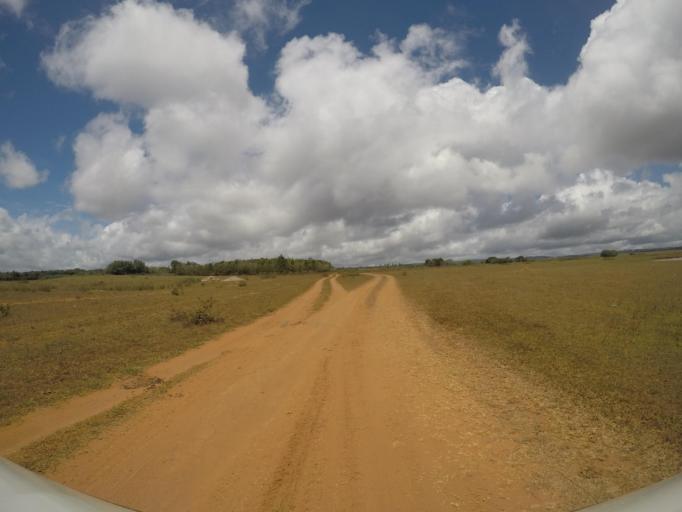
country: TL
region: Lautem
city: Lospalos
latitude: -8.4689
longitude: 126.9854
